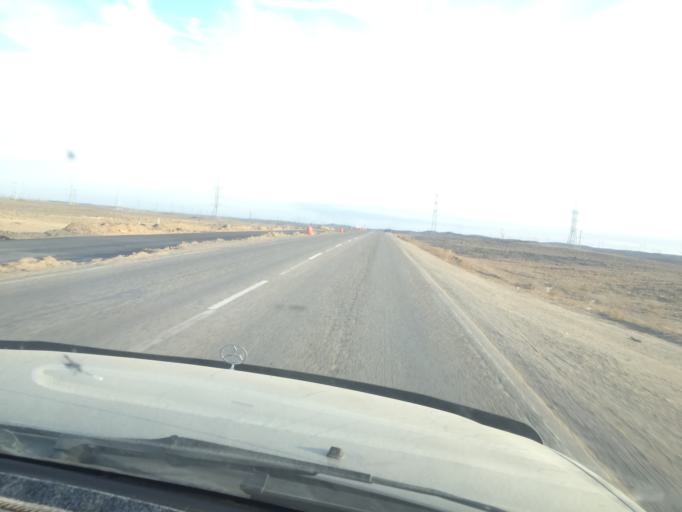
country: KZ
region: Almaty Oblysy
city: Ulken
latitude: 45.2149
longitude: 73.8696
